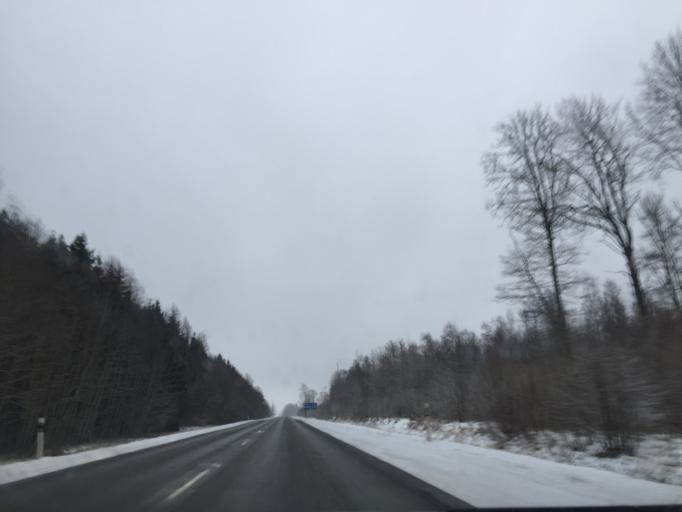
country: EE
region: Laeaene
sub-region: Lihula vald
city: Lihula
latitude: 58.5479
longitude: 23.9931
